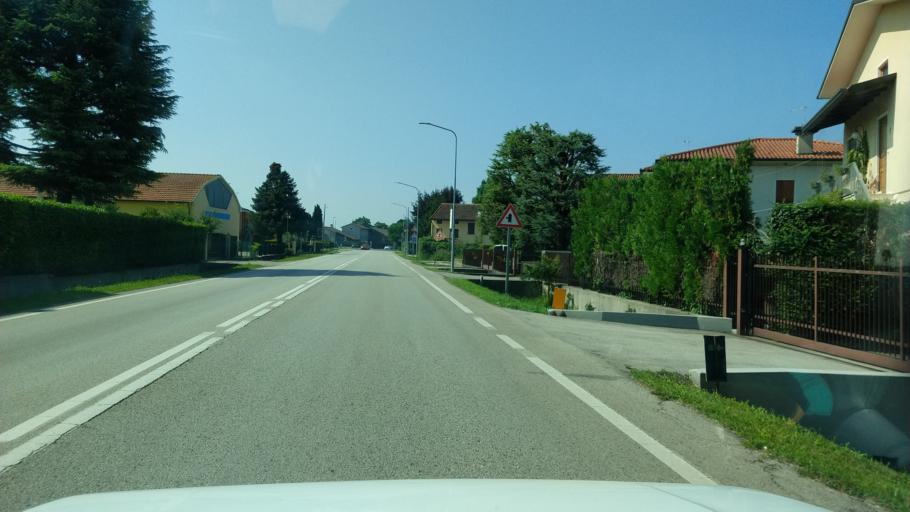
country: IT
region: Veneto
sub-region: Provincia di Vicenza
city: Bressanvido
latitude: 45.6661
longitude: 11.6355
